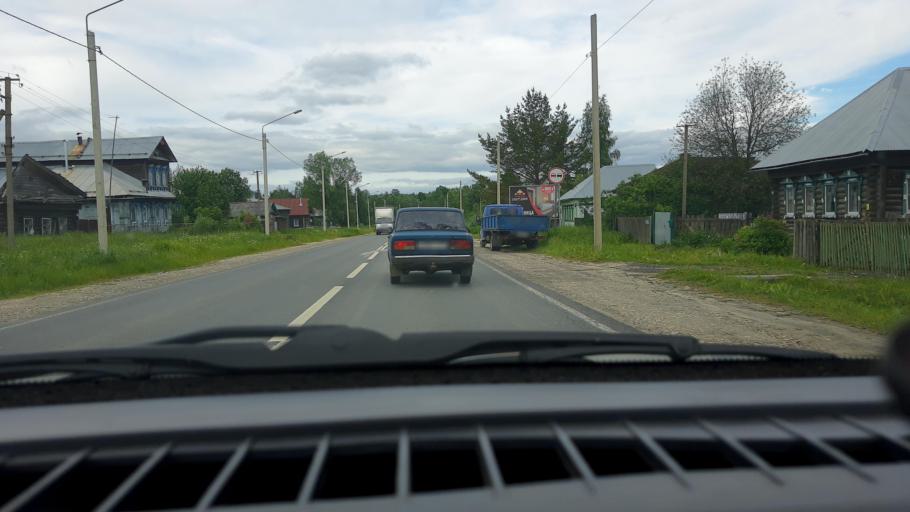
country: RU
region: Nizjnij Novgorod
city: Vladimirskoye
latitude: 56.8963
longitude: 45.0037
